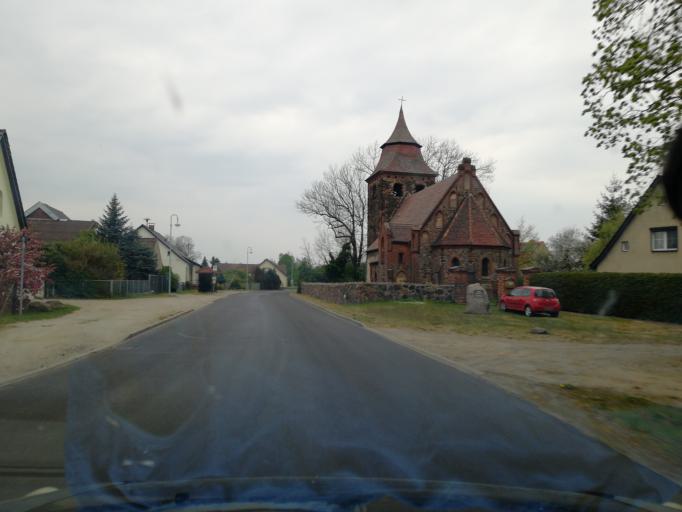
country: DE
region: Brandenburg
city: Calau
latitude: 51.7608
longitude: 13.9128
